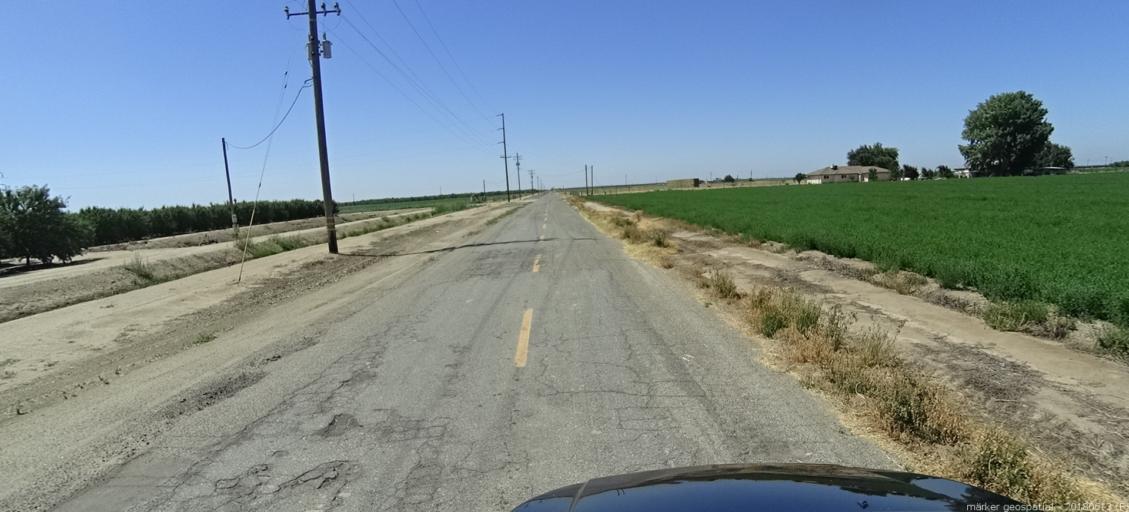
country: US
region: California
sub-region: Madera County
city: Chowchilla
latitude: 37.0592
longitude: -120.3469
